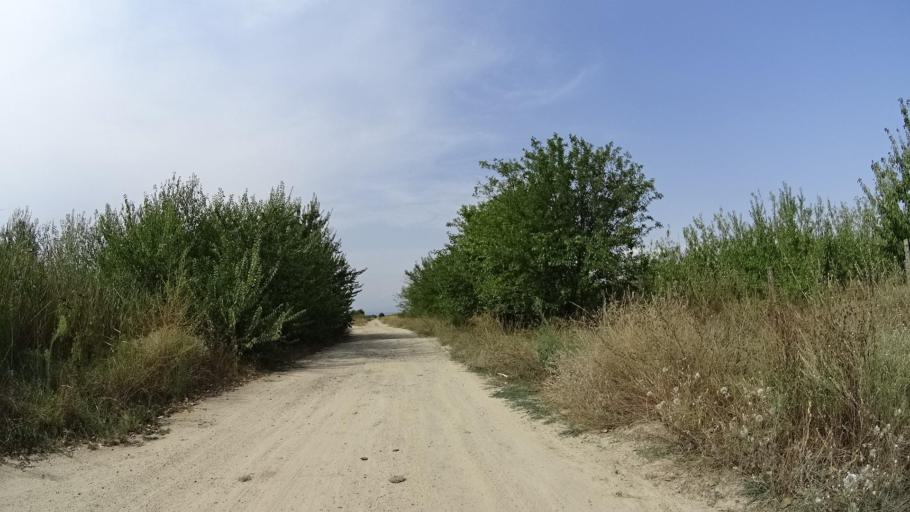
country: BG
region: Plovdiv
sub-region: Obshtina Kaloyanovo
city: Kaloyanovo
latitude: 42.2782
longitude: 24.7996
